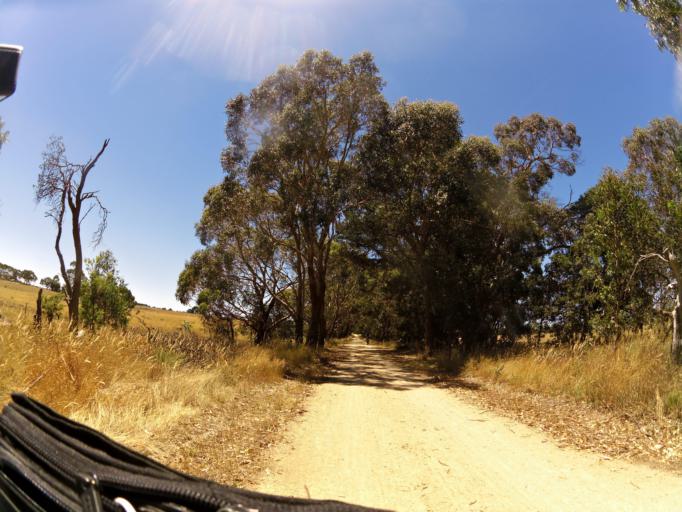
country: AU
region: Victoria
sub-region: Ballarat North
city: Delacombe
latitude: -37.5588
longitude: 143.7429
